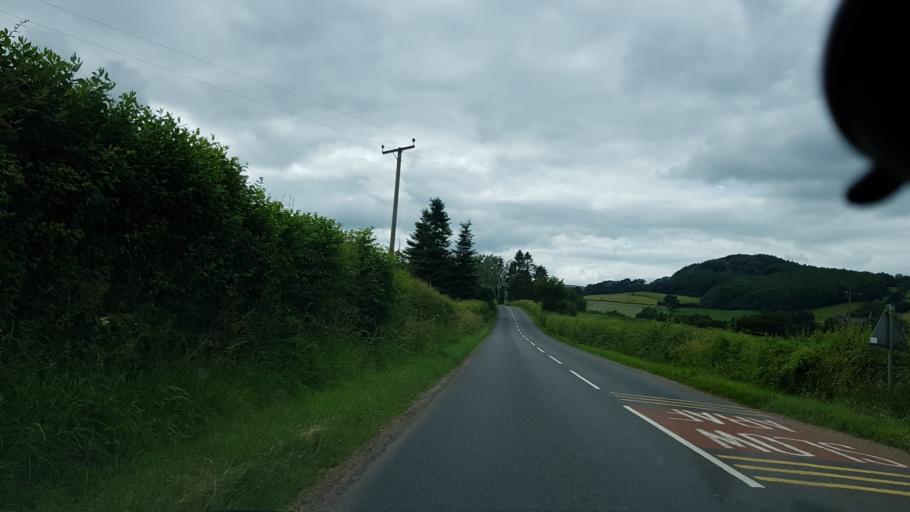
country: GB
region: England
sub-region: Herefordshire
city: Llanrothal
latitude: 51.8777
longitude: -2.7926
